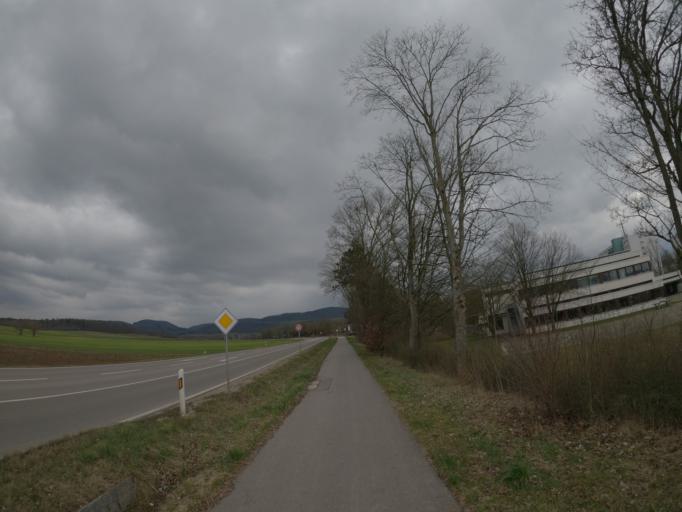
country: DE
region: Baden-Wuerttemberg
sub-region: Regierungsbezirk Stuttgart
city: Schlat
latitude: 48.6684
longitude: 9.6949
